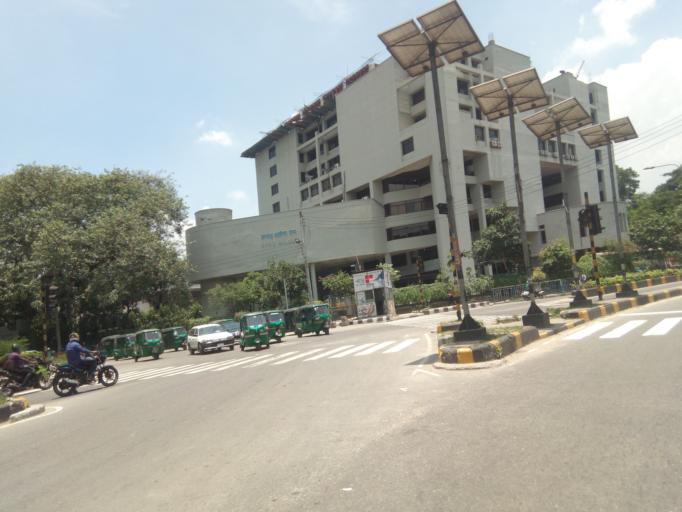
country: BD
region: Dhaka
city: Paltan
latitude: 23.7376
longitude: 90.4041
